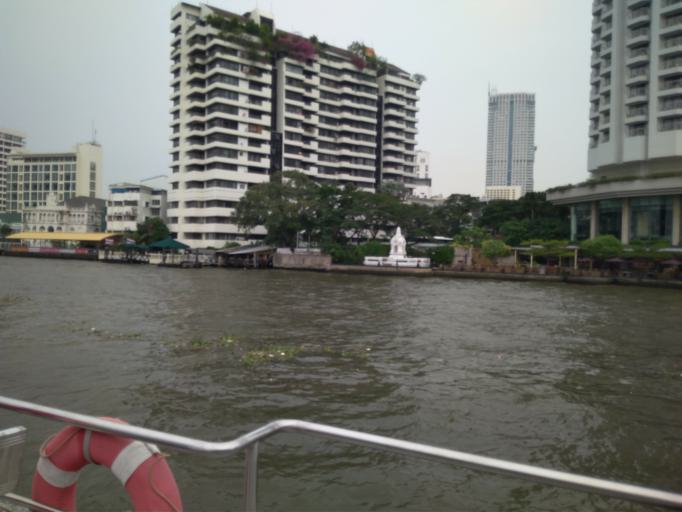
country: TH
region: Bangkok
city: Samphanthawong
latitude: 13.7219
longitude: 100.5128
